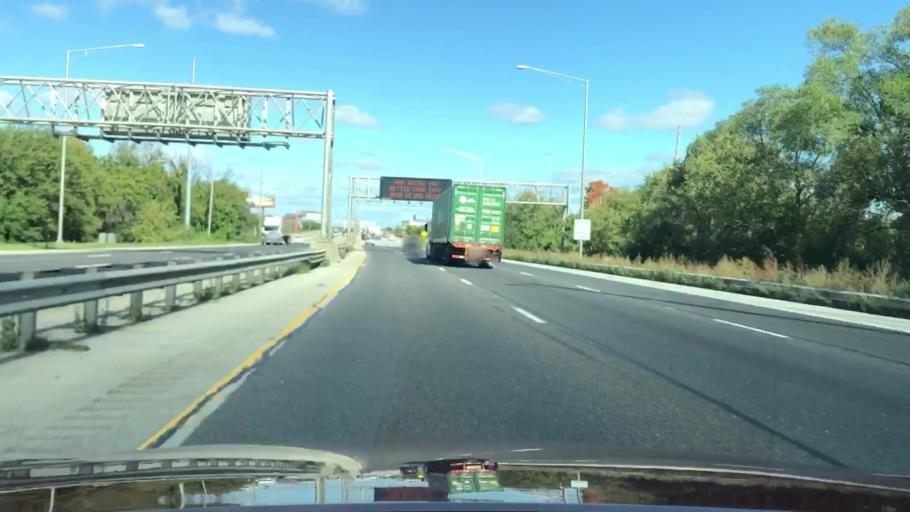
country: US
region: Illinois
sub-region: Cook County
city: Burnham
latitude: 41.6309
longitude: -87.5783
